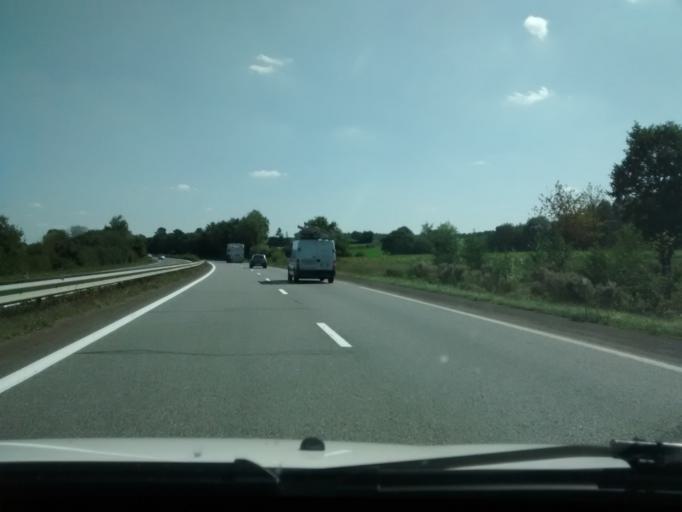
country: FR
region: Brittany
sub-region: Departement des Cotes-d'Armor
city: Broons
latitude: 48.2981
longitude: -2.2298
